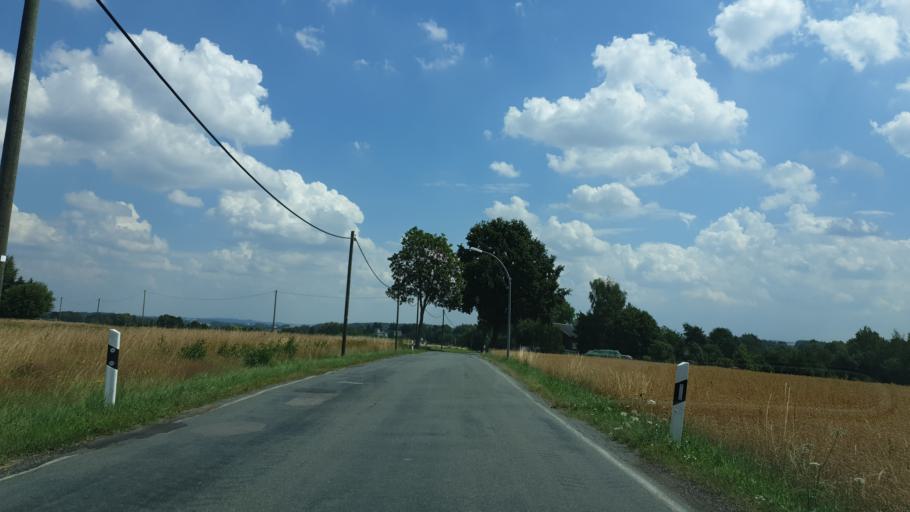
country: DE
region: Saxony
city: Kirchberg
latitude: 50.7982
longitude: 12.7801
